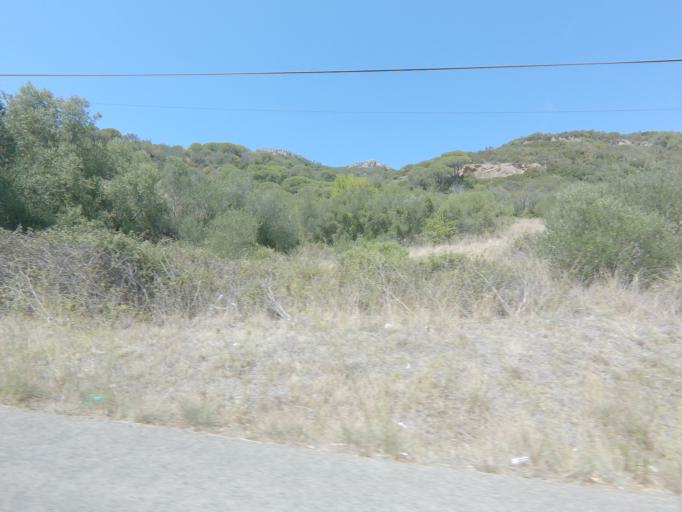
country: PT
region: Setubal
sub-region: Palmela
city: Quinta do Anjo
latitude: 38.5272
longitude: -8.9309
